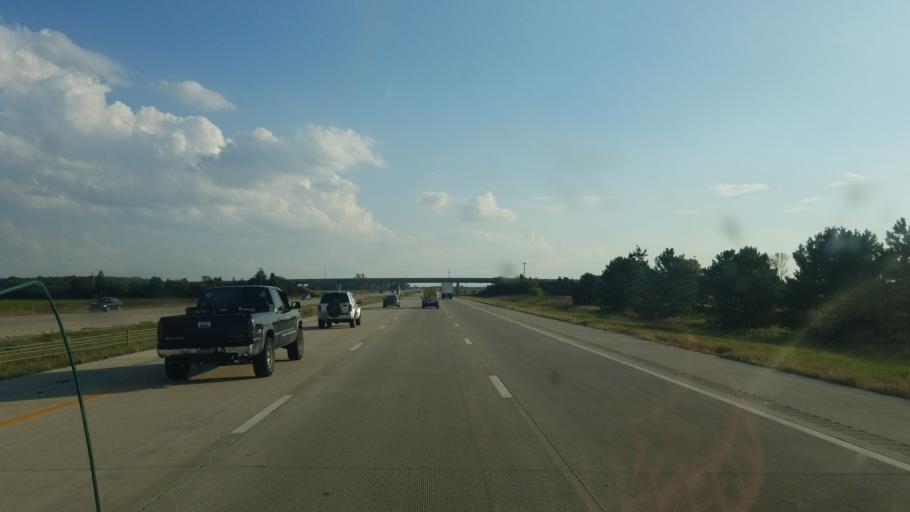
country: US
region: Ohio
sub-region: Wood County
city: Perrysburg
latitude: 41.4954
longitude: -83.6222
